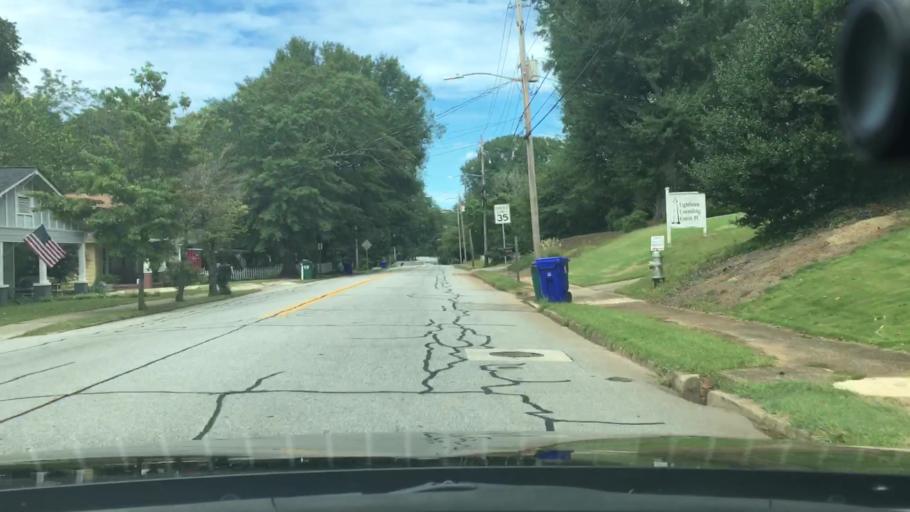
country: US
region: Georgia
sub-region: Coweta County
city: Newnan
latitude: 33.3836
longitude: -84.8001
